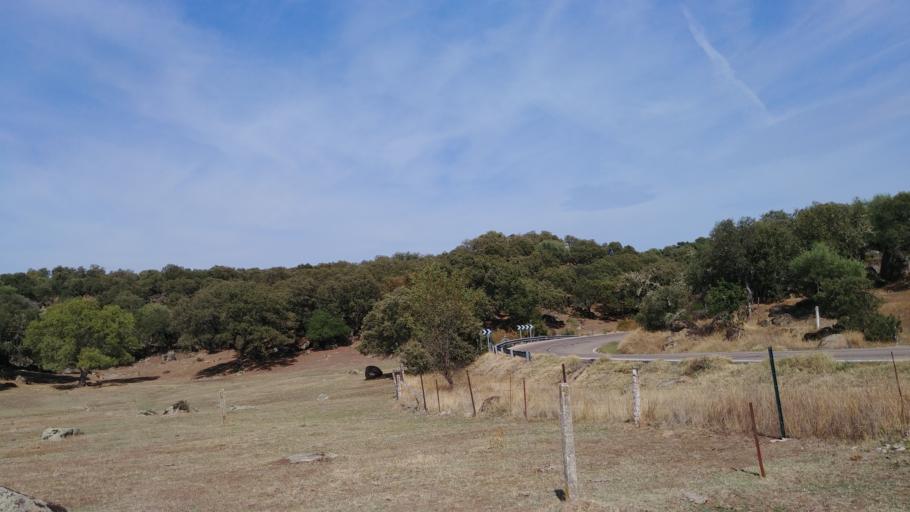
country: ES
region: Castille-La Mancha
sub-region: Province of Toledo
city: Navalcan
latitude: 40.0517
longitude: -5.1371
